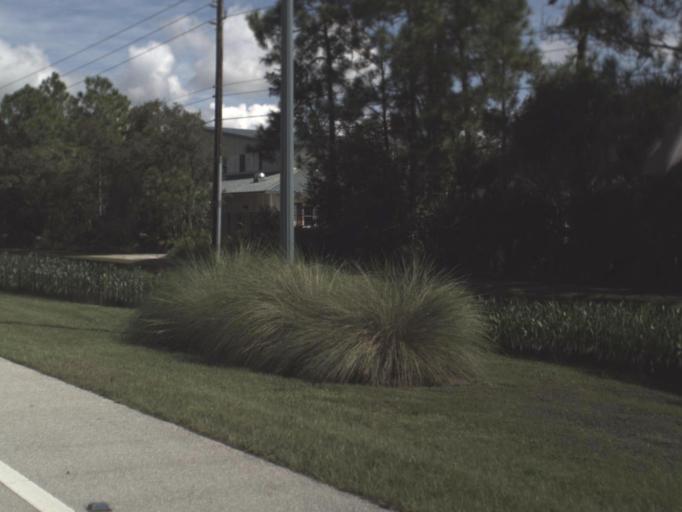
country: US
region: Florida
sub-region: Sarasota County
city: North Port
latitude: 27.0817
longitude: -82.1555
